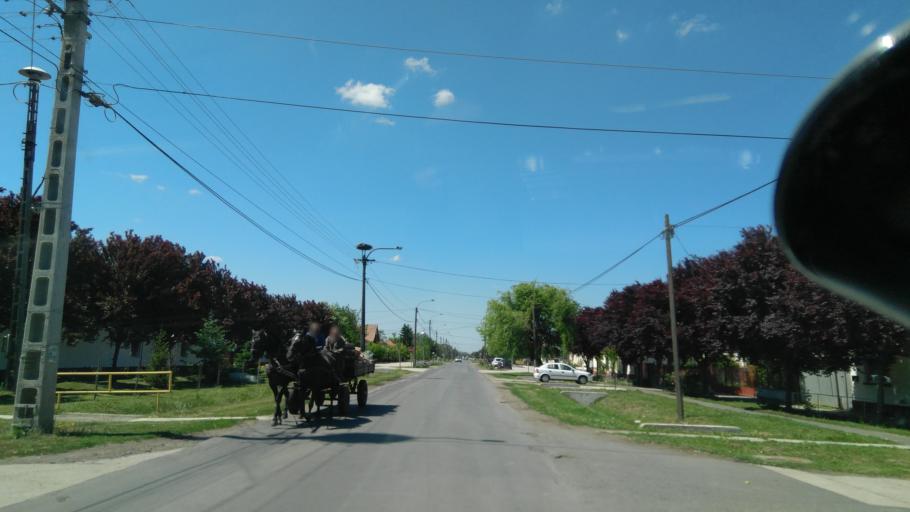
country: HU
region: Bekes
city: Kunagota
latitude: 46.4248
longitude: 21.0499
